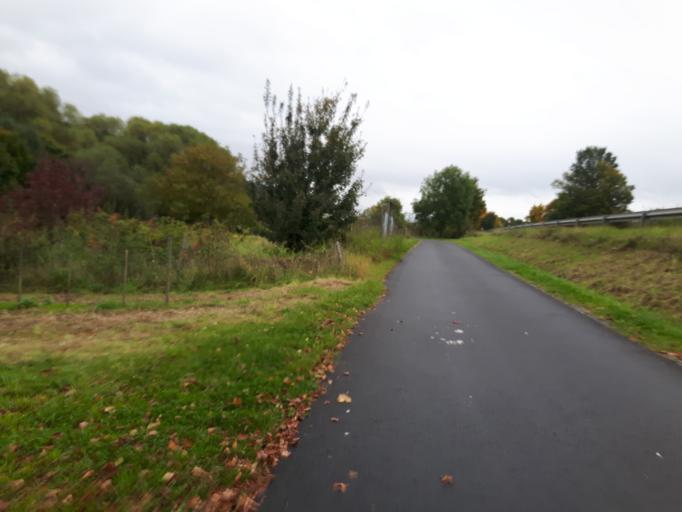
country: DE
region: Bavaria
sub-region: Regierungsbezirk Unterfranken
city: Erlabrunn
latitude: 49.8590
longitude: 9.8471
